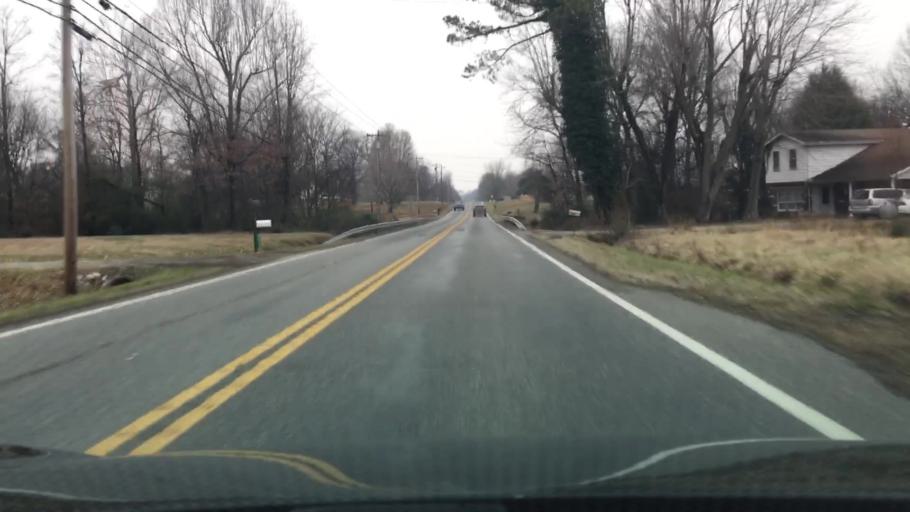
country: US
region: Kentucky
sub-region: Livingston County
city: Ledbetter
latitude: 36.9700
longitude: -88.4609
